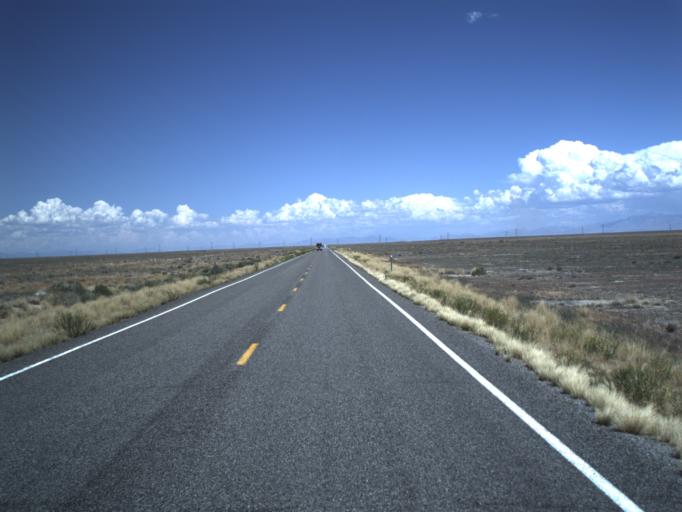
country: US
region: Utah
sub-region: Millard County
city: Delta
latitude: 39.2194
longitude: -112.9505
